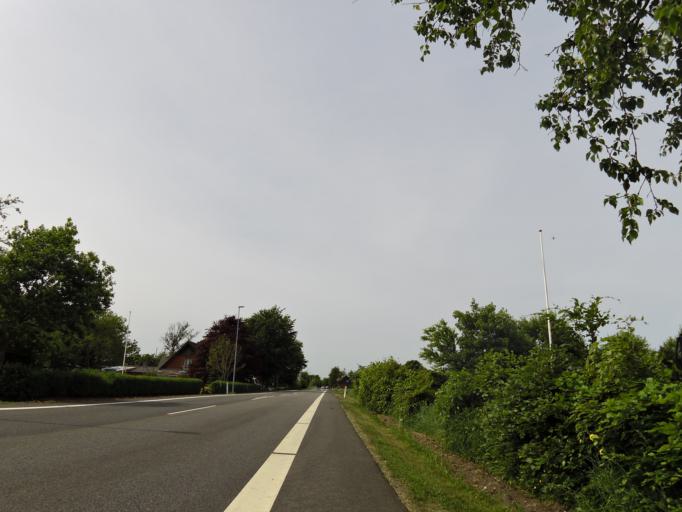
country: DK
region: Central Jutland
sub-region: Holstebro Kommune
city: Vinderup
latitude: 56.5727
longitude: 8.8608
